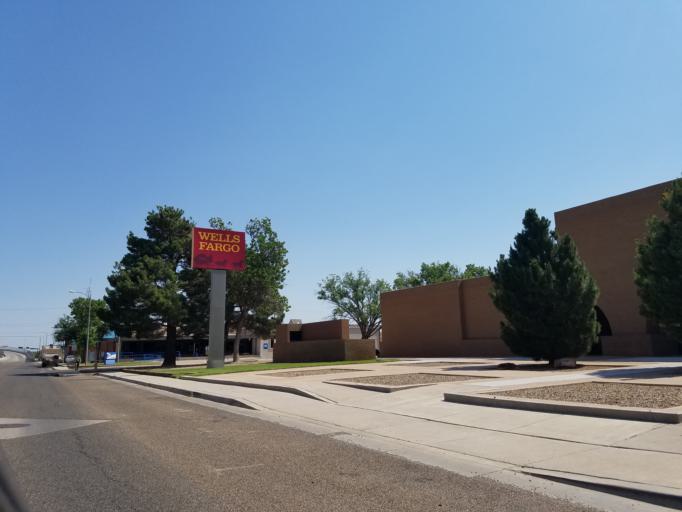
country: US
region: New Mexico
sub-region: Quay County
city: Tucumcari
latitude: 35.1757
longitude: -103.7249
